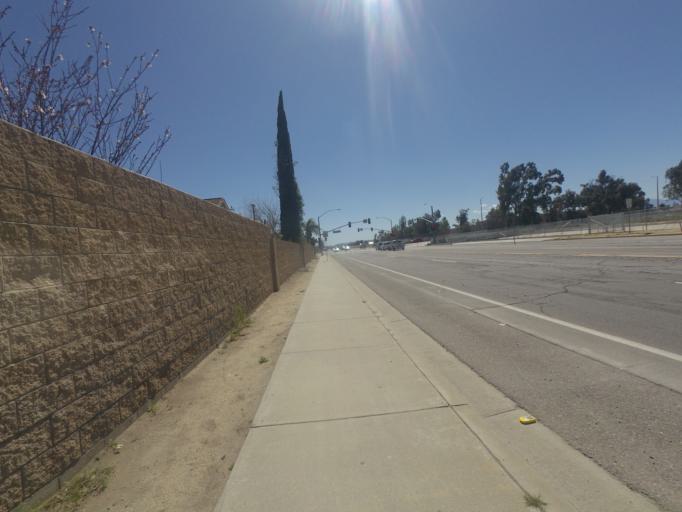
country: US
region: California
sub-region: Riverside County
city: March Air Force Base
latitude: 33.9037
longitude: -117.2435
